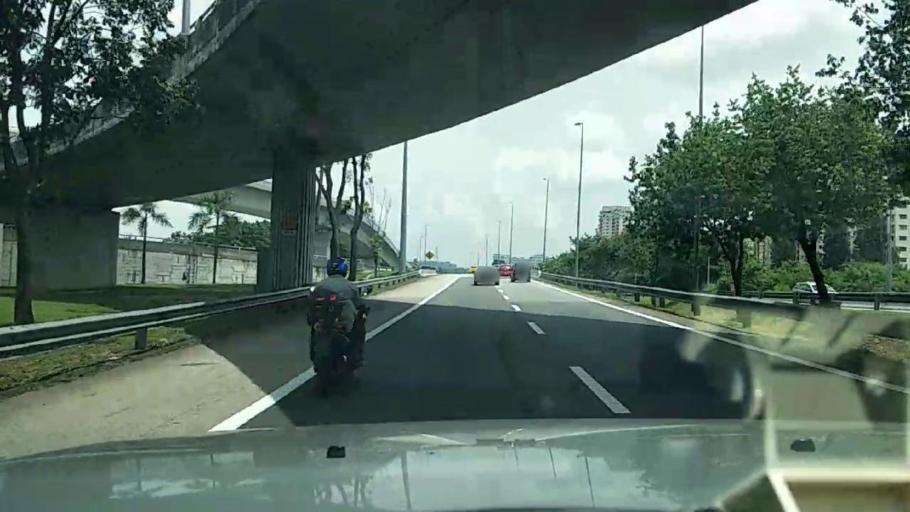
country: MY
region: Kuala Lumpur
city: Kuala Lumpur
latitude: 3.0944
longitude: 101.6900
